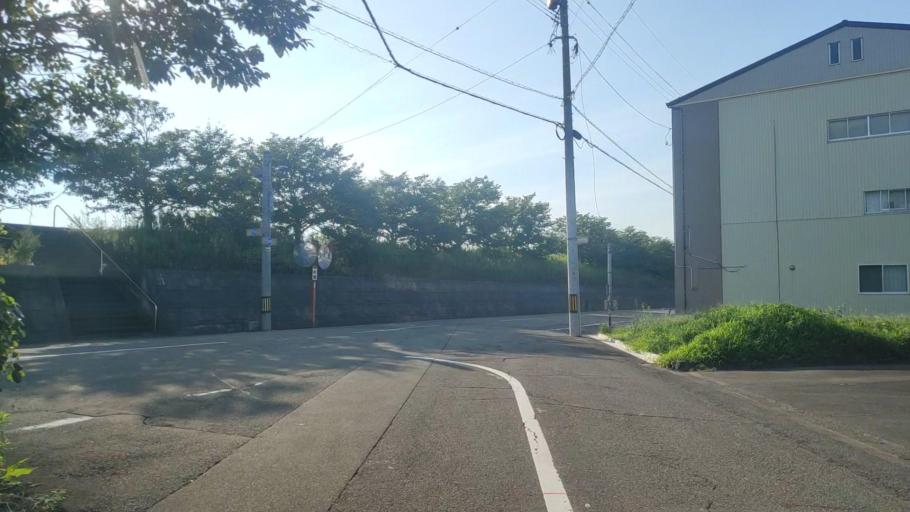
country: JP
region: Fukui
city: Fukui-shi
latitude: 36.0521
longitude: 136.2321
